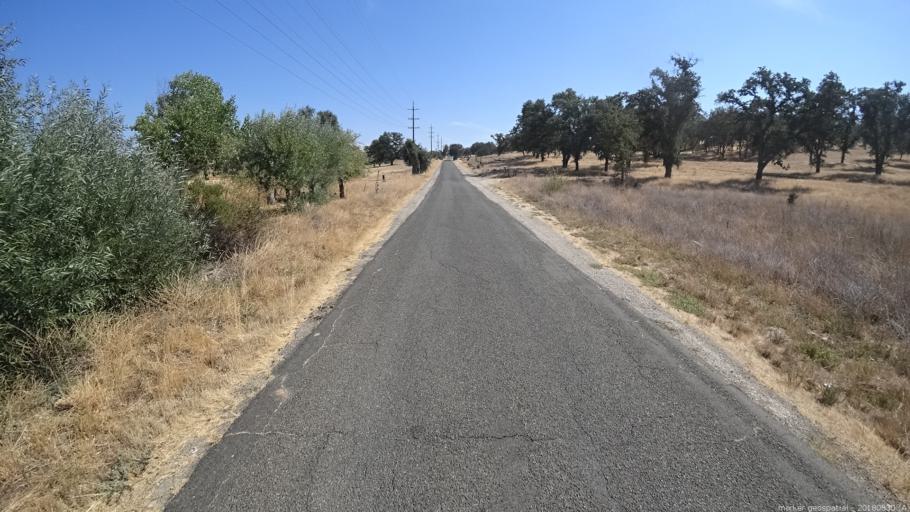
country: US
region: California
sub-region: Monterey County
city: King City
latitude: 36.0169
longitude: -121.1695
